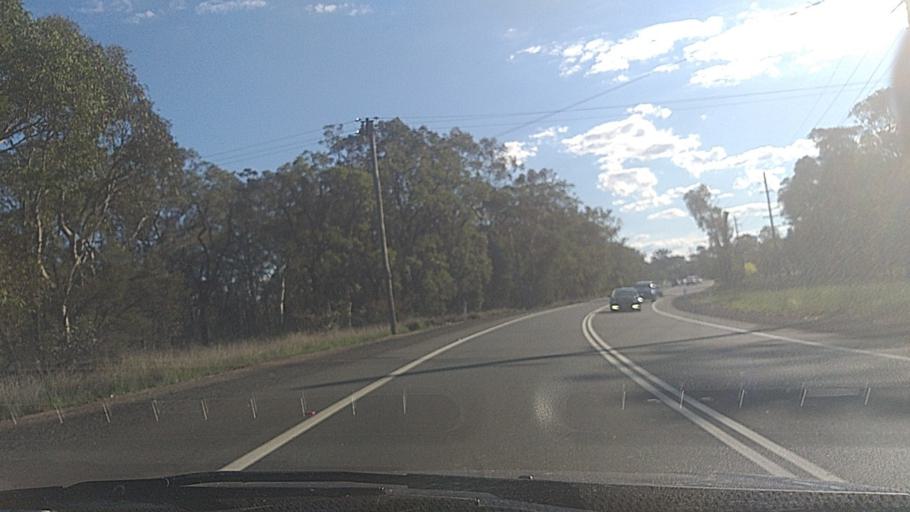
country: AU
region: New South Wales
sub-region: Hawkesbury
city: South Windsor
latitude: -33.6570
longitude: 150.7696
